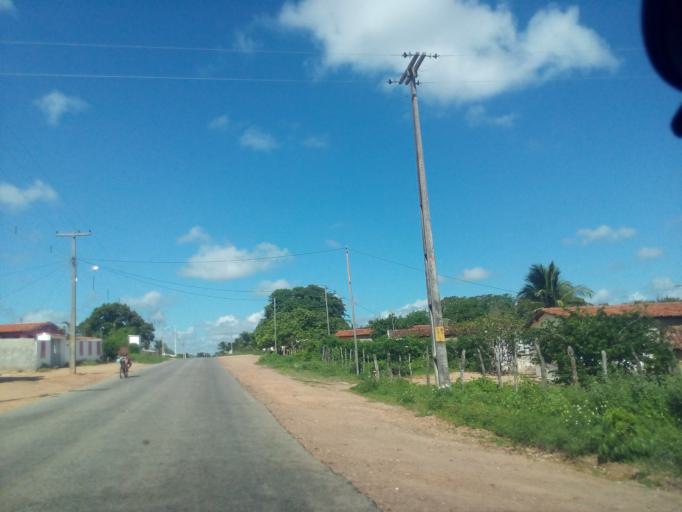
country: BR
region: Rio Grande do Norte
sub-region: Sao Paulo Do Potengi
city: Sao Paulo do Potengi
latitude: -5.9130
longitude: -35.7040
